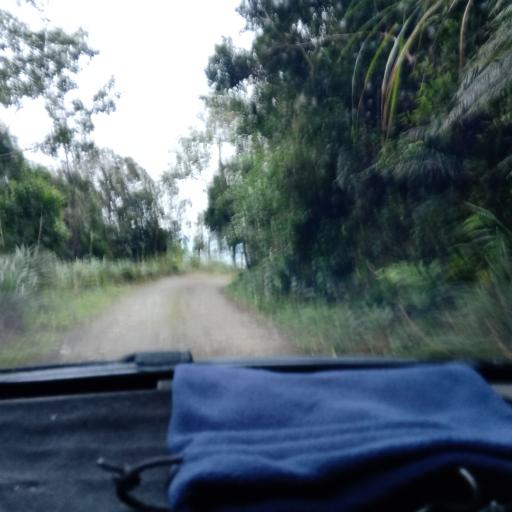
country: TW
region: Taiwan
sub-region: Yilan
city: Yilan
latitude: 24.8113
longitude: 121.6914
